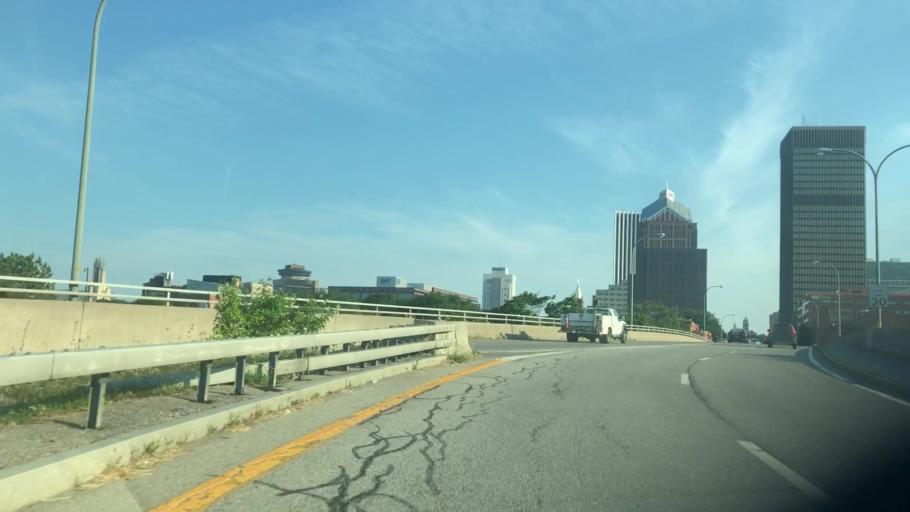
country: US
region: New York
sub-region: Monroe County
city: Rochester
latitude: 43.1499
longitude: -77.6041
